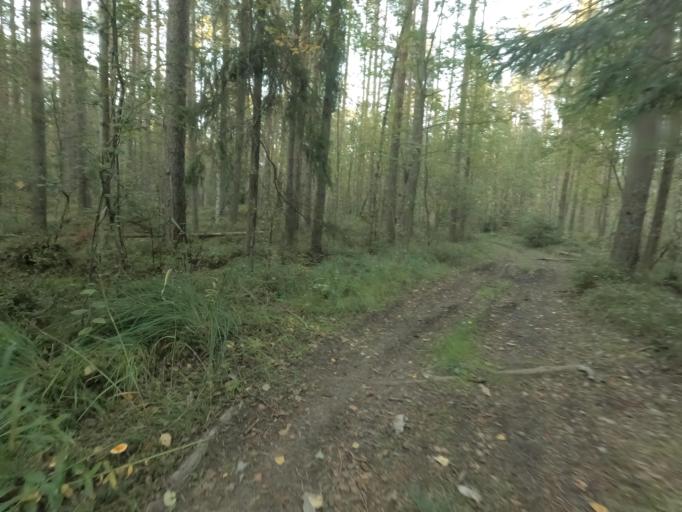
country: RU
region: Leningrad
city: Otradnoye
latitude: 59.8268
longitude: 30.8230
